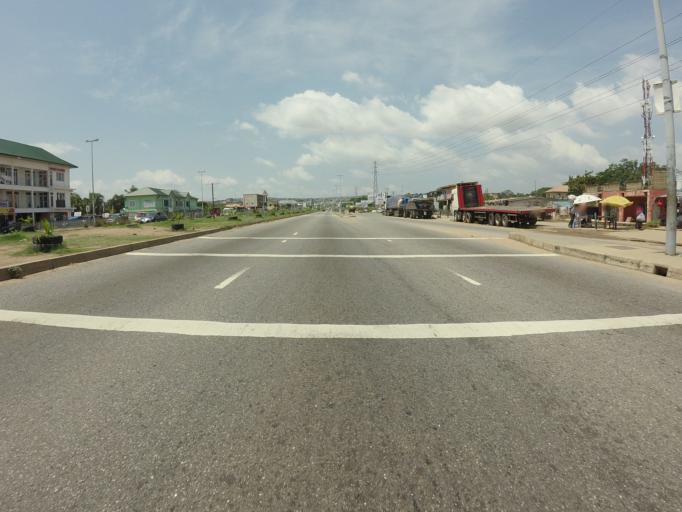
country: GH
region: Greater Accra
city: Gbawe
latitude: 5.5885
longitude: -0.2815
